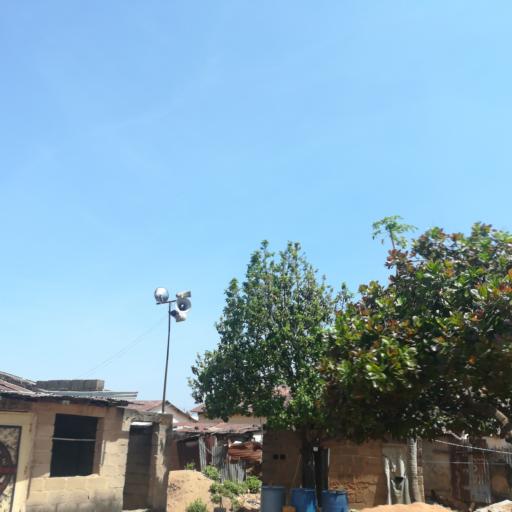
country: NG
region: Plateau
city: Bukuru
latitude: 9.8000
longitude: 8.8606
